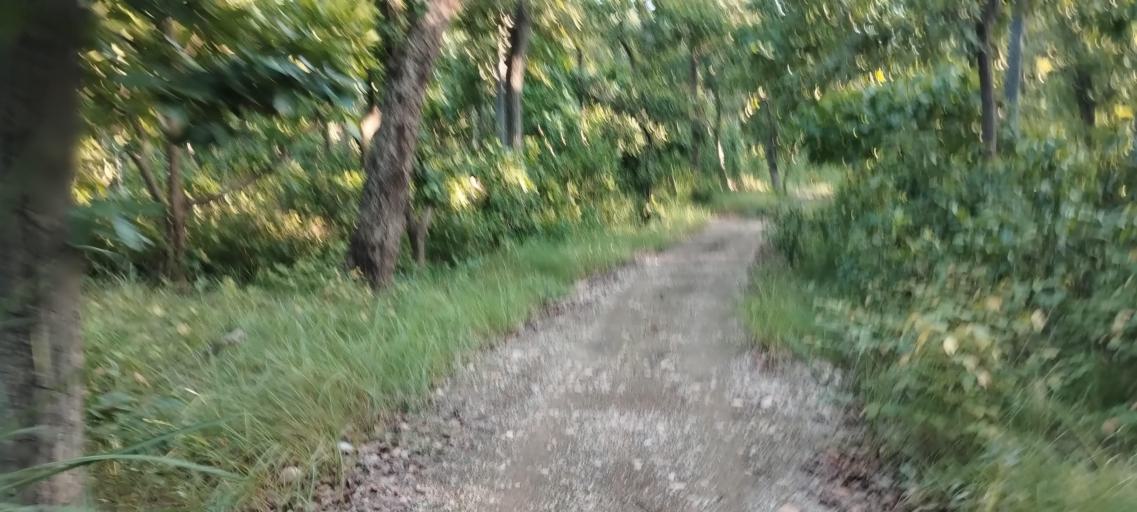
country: NP
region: Far Western
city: Tikapur
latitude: 28.4913
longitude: 81.2552
